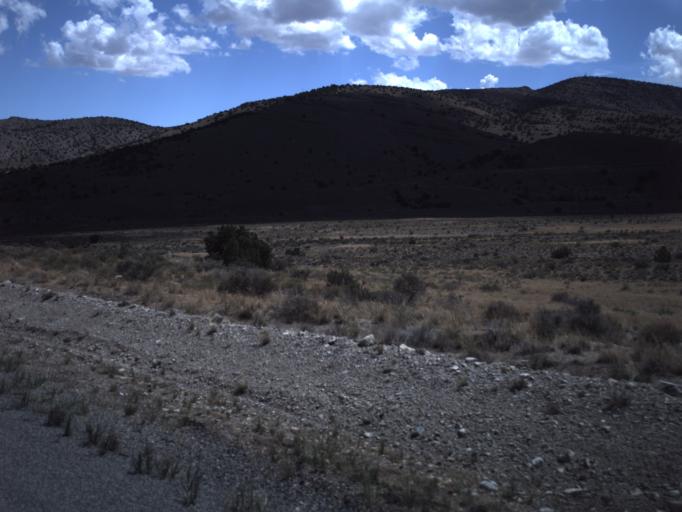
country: US
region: Utah
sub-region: Beaver County
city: Milford
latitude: 39.0781
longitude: -113.6157
